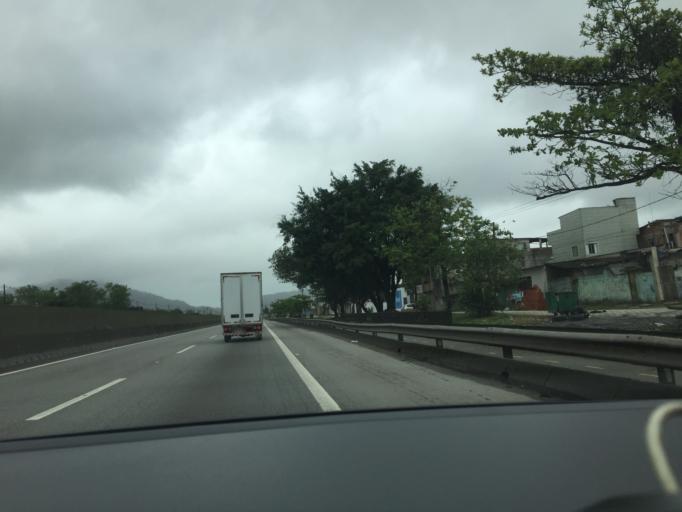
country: BR
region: Sao Paulo
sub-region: Guaruja
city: Guaruja
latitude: -23.9557
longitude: -46.2754
